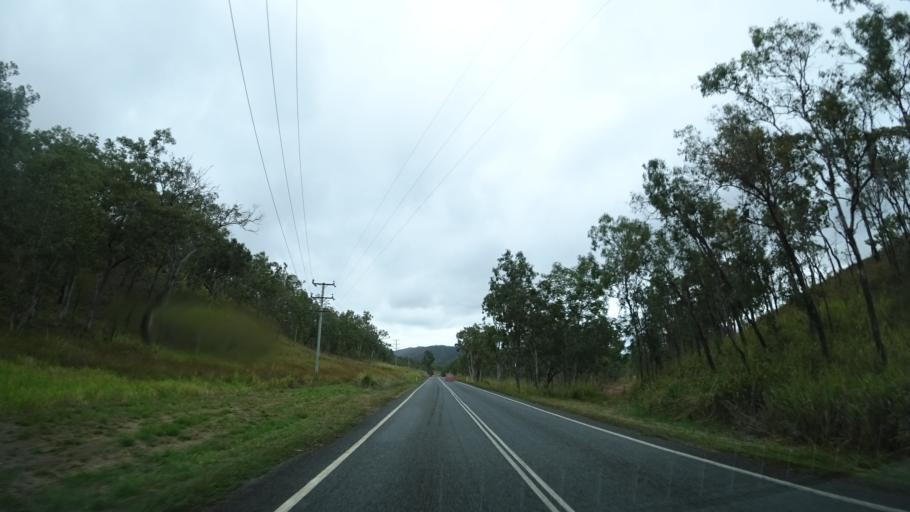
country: AU
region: Queensland
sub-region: Cairns
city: Port Douglas
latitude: -16.7078
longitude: 145.3492
